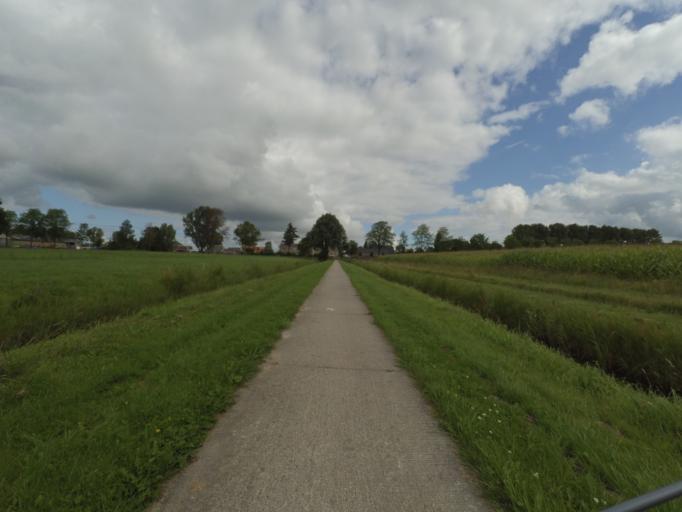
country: NL
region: Friesland
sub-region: Gemeente Kollumerland en Nieuwkruisland
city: Kollum
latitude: 53.2940
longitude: 6.2322
